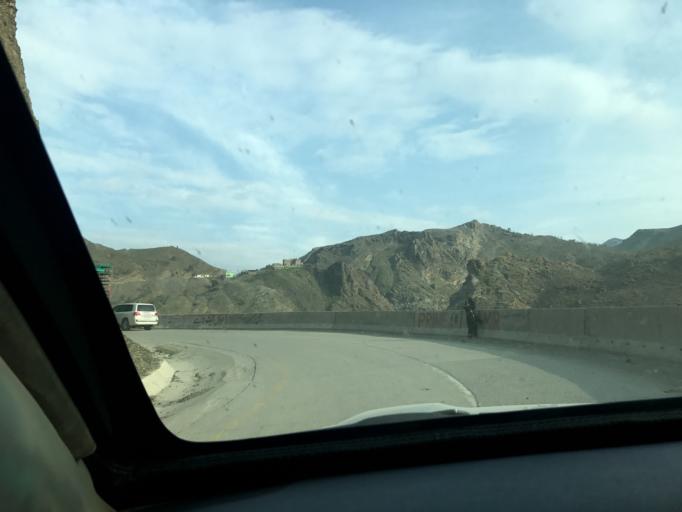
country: PK
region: Federally Administered Tribal Areas
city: Landi Kotal
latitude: 34.1113
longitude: 71.1129
